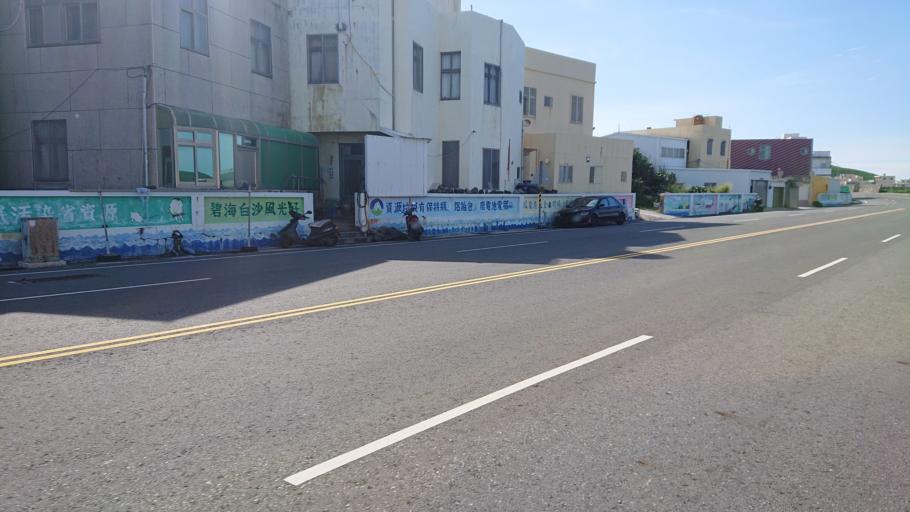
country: TW
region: Taiwan
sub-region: Penghu
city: Ma-kung
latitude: 23.5221
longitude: 119.5732
